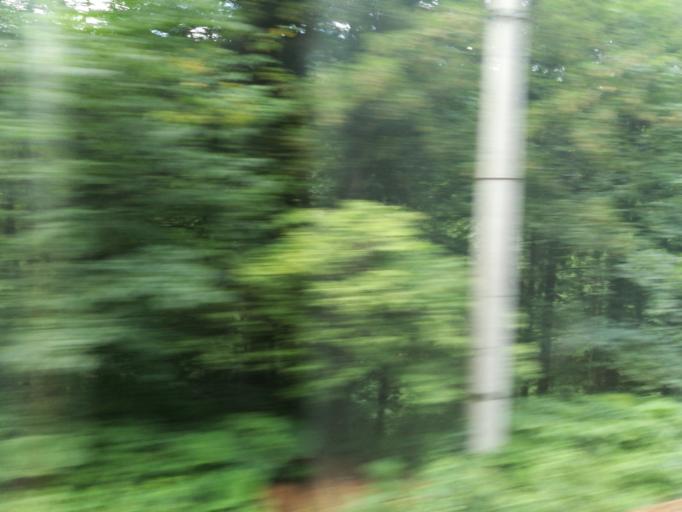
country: RO
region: Brasov
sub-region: Oras Predeal
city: Predeal
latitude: 45.5197
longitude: 25.5979
